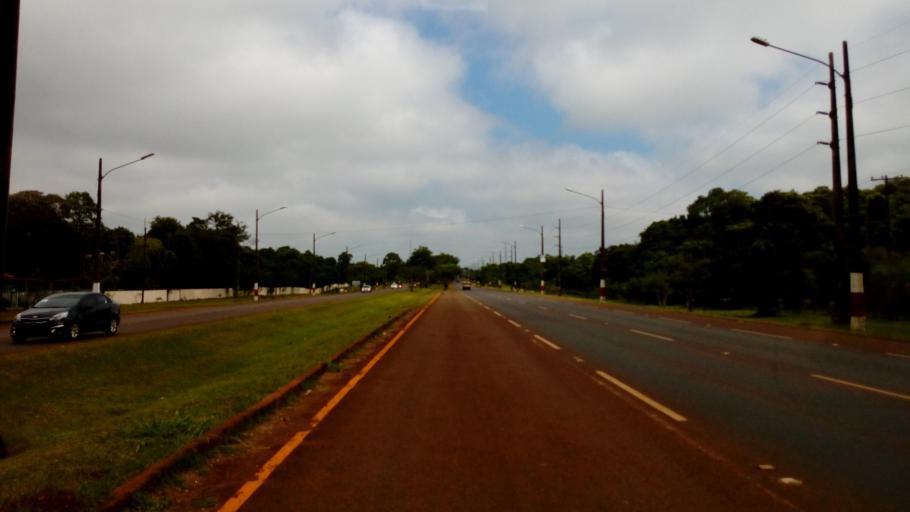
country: PY
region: Alto Parana
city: Ciudad del Este
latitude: -25.4409
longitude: -54.6341
